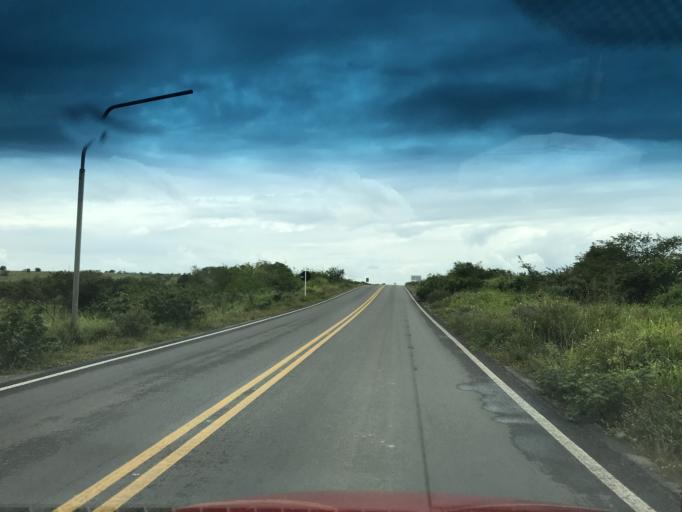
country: BR
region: Bahia
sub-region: Castro Alves
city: Castro Alves
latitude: -12.7567
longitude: -39.4145
